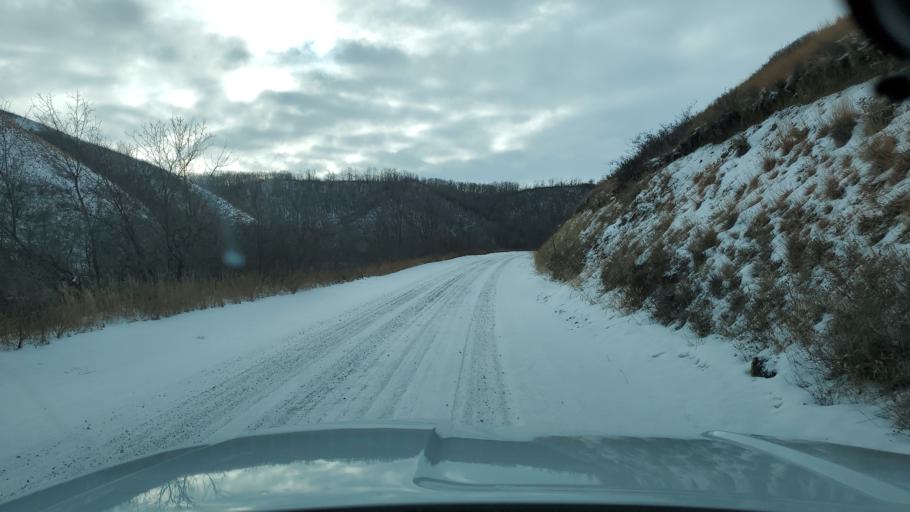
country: CA
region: Saskatchewan
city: White City
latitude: 50.7736
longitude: -104.1423
